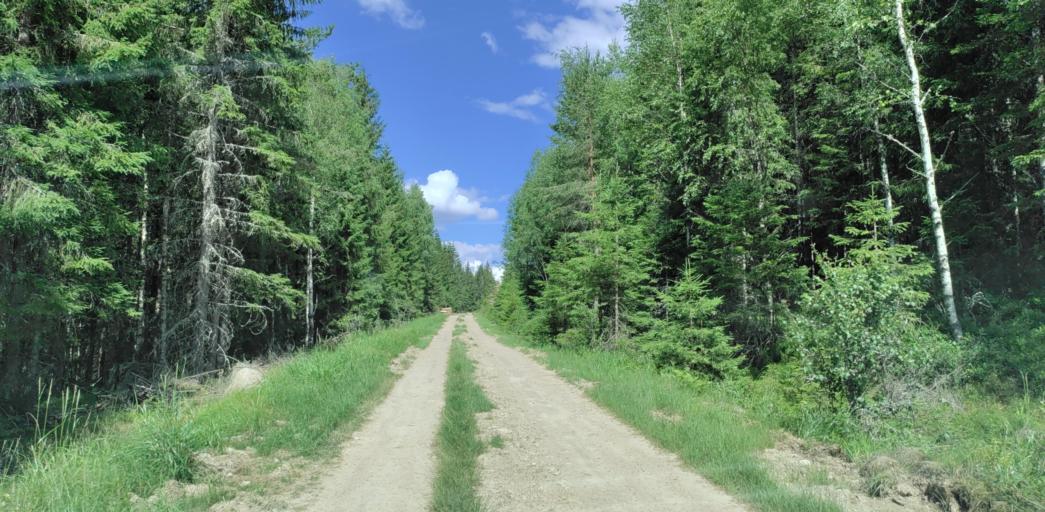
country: SE
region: Vaermland
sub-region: Hagfors Kommun
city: Ekshaerad
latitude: 60.0657
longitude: 13.3405
